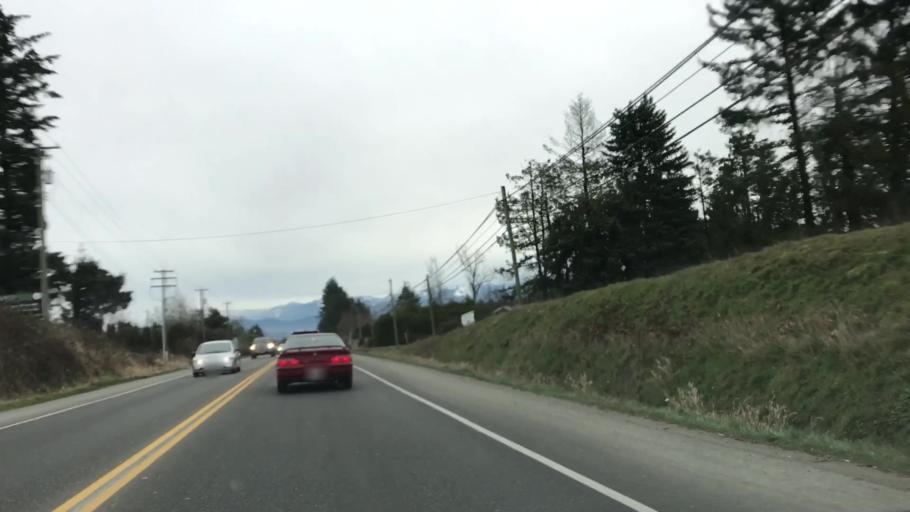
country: CA
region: British Columbia
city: Aldergrove
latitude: 49.0574
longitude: -122.3990
